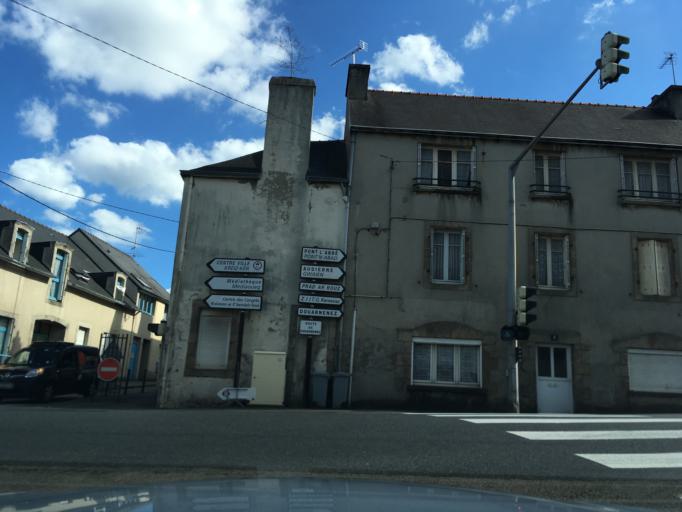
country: FR
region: Brittany
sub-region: Departement du Finistere
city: Quimper
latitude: 48.0003
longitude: -4.1125
